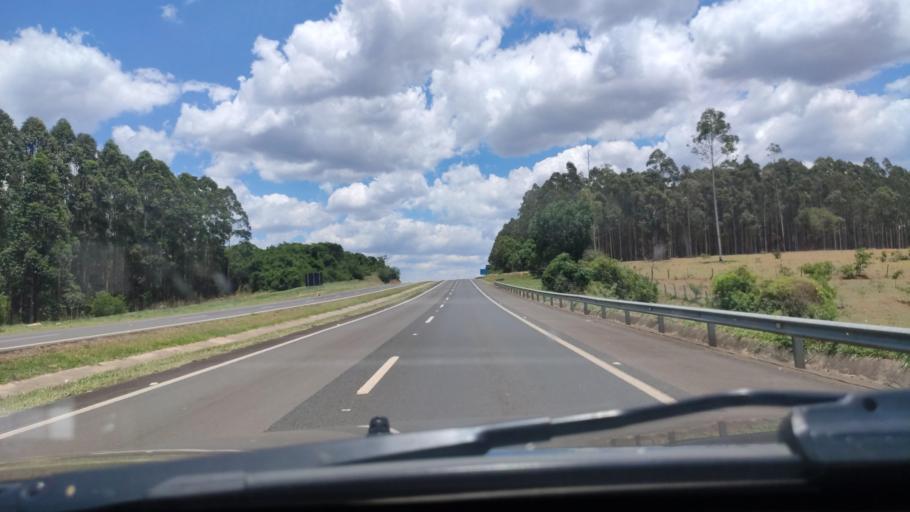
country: BR
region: Sao Paulo
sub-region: Duartina
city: Duartina
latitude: -22.4934
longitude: -49.2574
